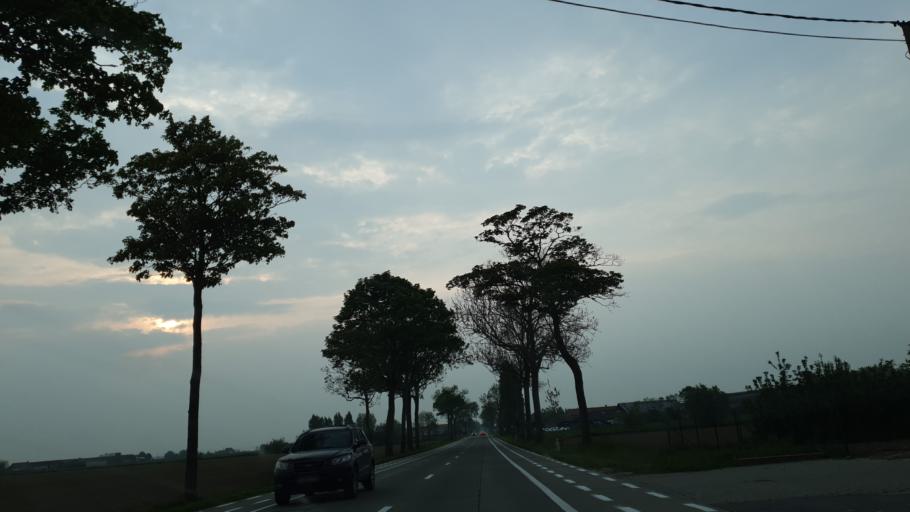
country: BE
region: Flanders
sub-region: Provincie West-Vlaanderen
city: Poperinge
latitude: 50.9144
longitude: 2.7665
